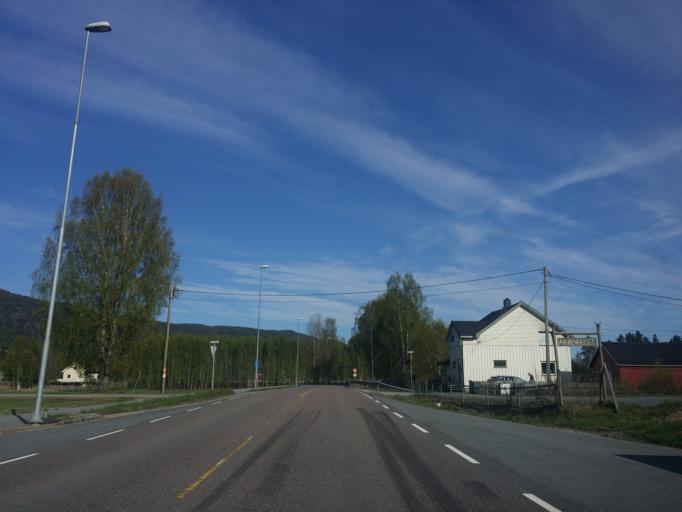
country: NO
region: Telemark
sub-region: Notodden
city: Notodden
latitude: 59.5923
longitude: 9.1480
